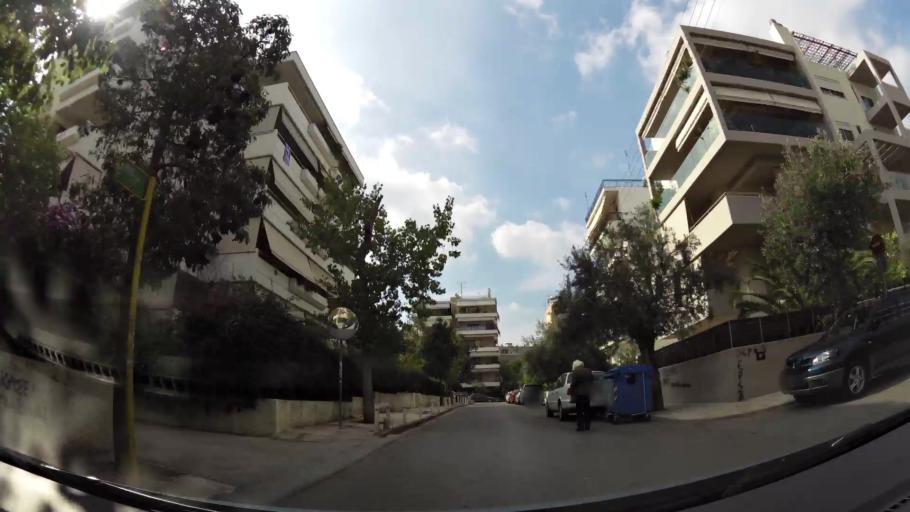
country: GR
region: Attica
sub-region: Nomarchia Athinas
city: Cholargos
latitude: 38.0030
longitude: 23.8004
